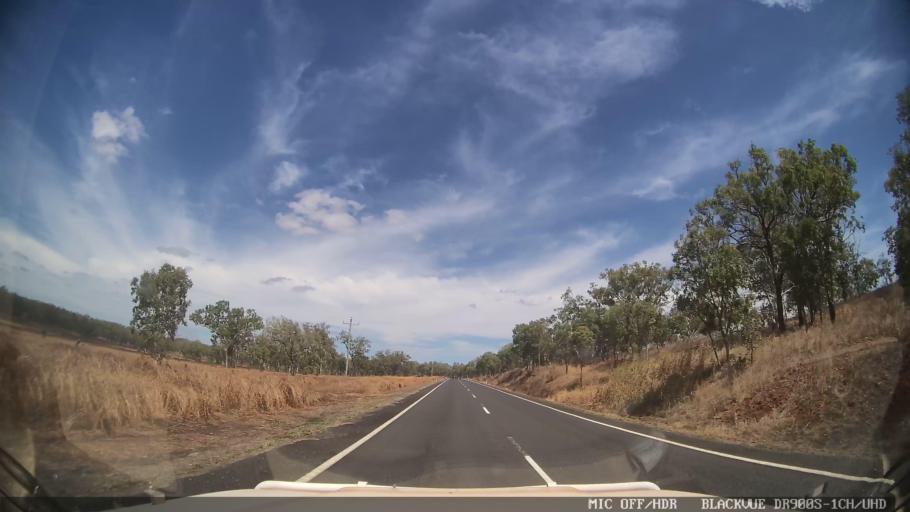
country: AU
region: Queensland
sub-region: Cook
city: Cooktown
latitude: -15.7982
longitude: 144.9251
